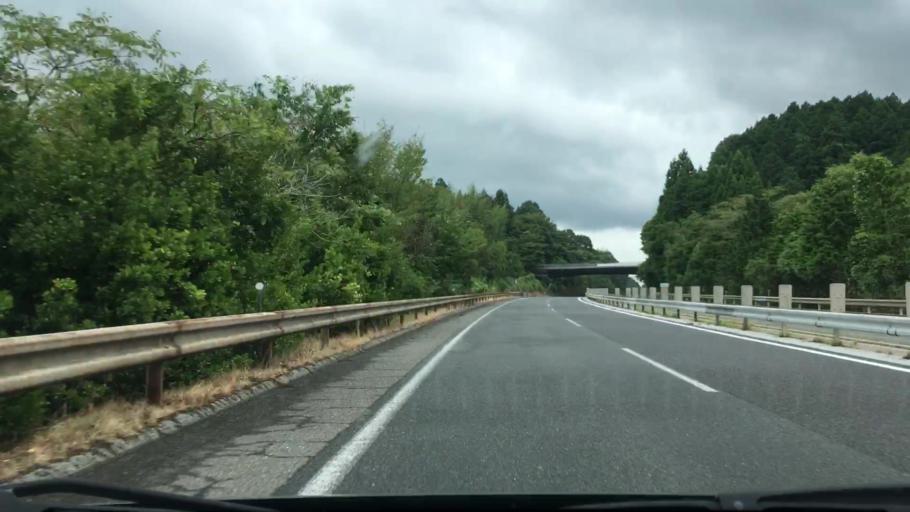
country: JP
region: Okayama
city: Niimi
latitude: 34.9281
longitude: 133.3260
